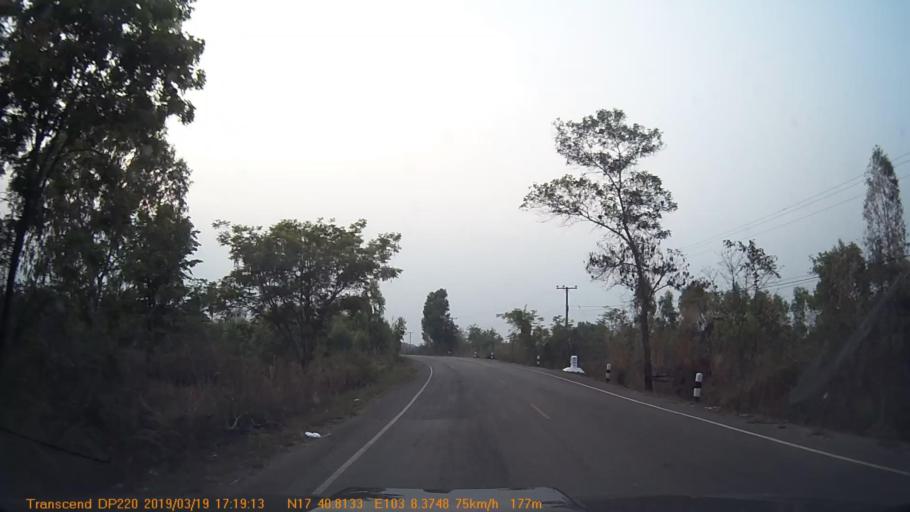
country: TH
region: Changwat Udon Thani
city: Ban Dung
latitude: 17.6805
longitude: 103.1391
